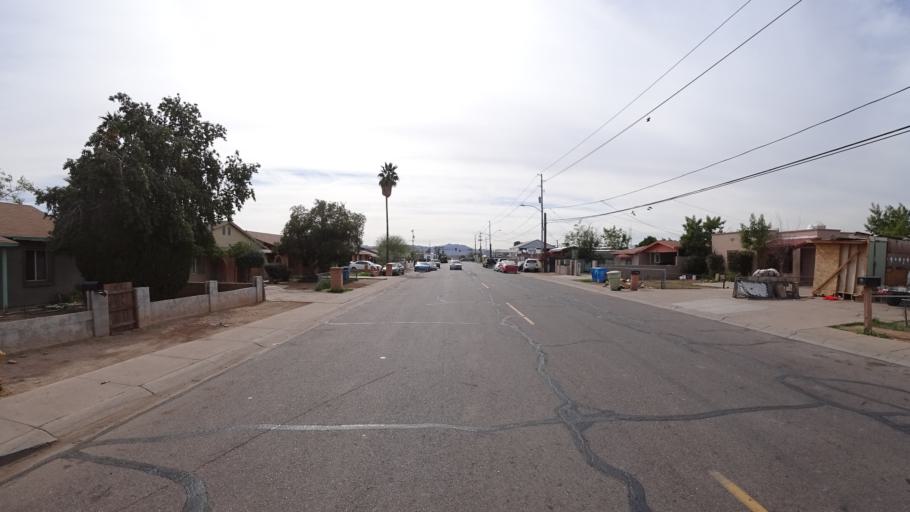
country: US
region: Arizona
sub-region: Maricopa County
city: Phoenix
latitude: 33.4385
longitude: -112.1260
